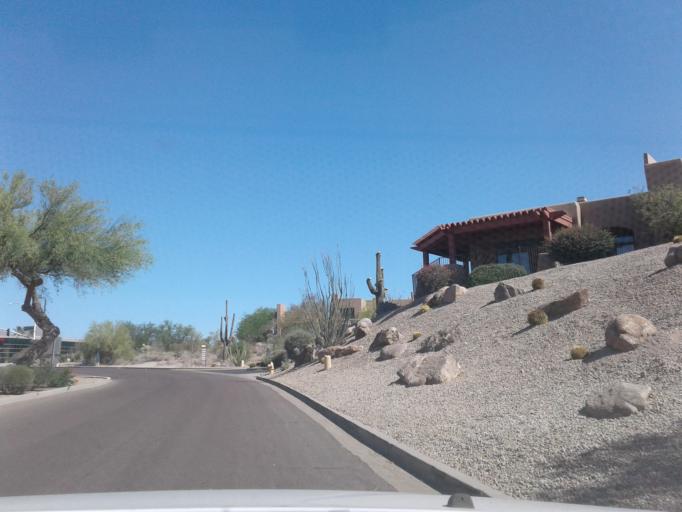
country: US
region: Arizona
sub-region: Maricopa County
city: Fountain Hills
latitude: 33.6060
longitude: -111.7128
